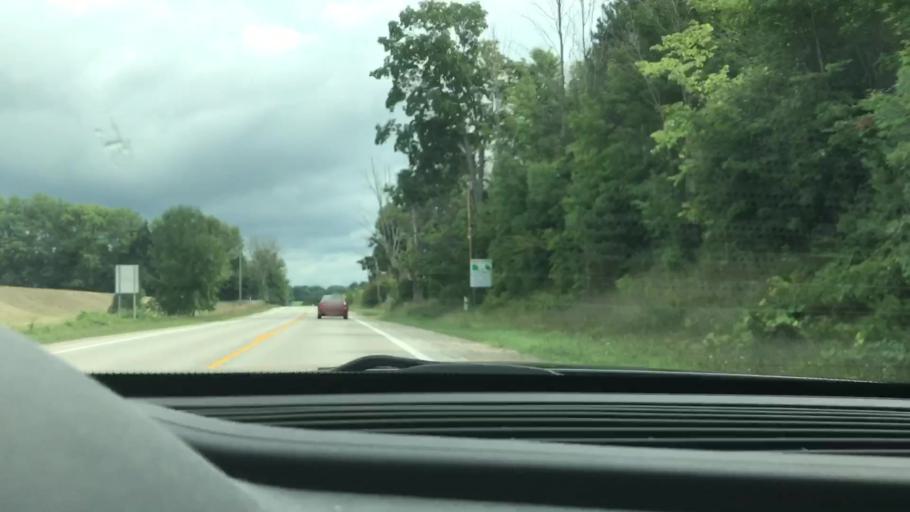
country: US
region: Michigan
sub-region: Antrim County
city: Bellaire
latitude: 45.0950
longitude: -85.2956
